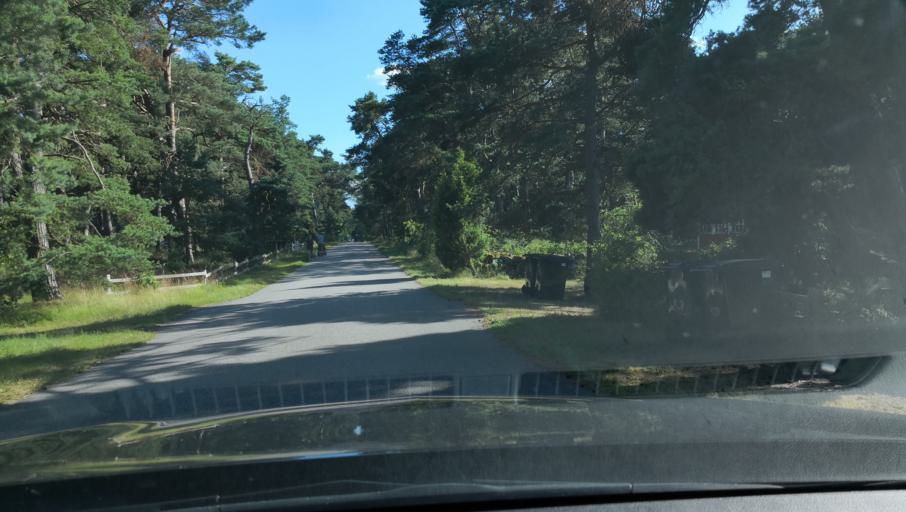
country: SE
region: Skane
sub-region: Simrishamns Kommun
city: Kivik
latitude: 55.7702
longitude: 14.1960
